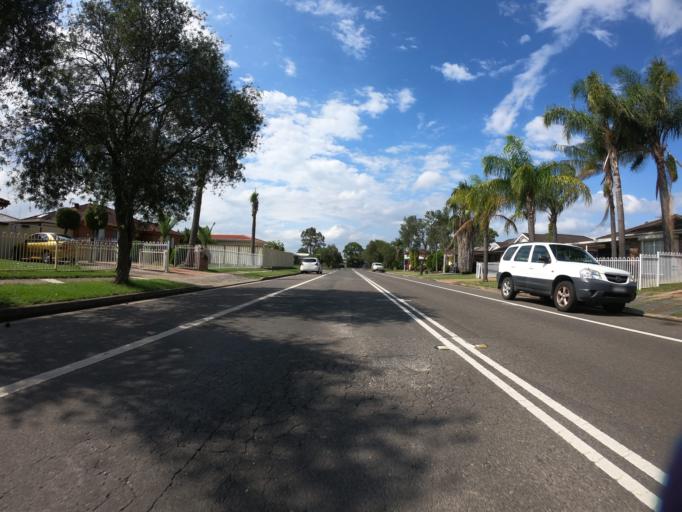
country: AU
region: New South Wales
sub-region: Blacktown
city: Hassall Grove
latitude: -33.7417
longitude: 150.8311
